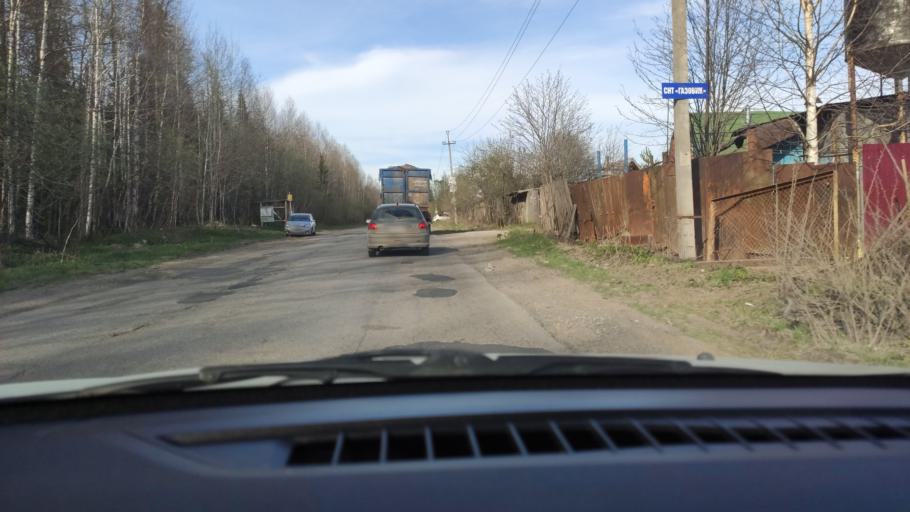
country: RU
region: Perm
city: Novyye Lyady
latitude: 57.9376
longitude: 56.4876
